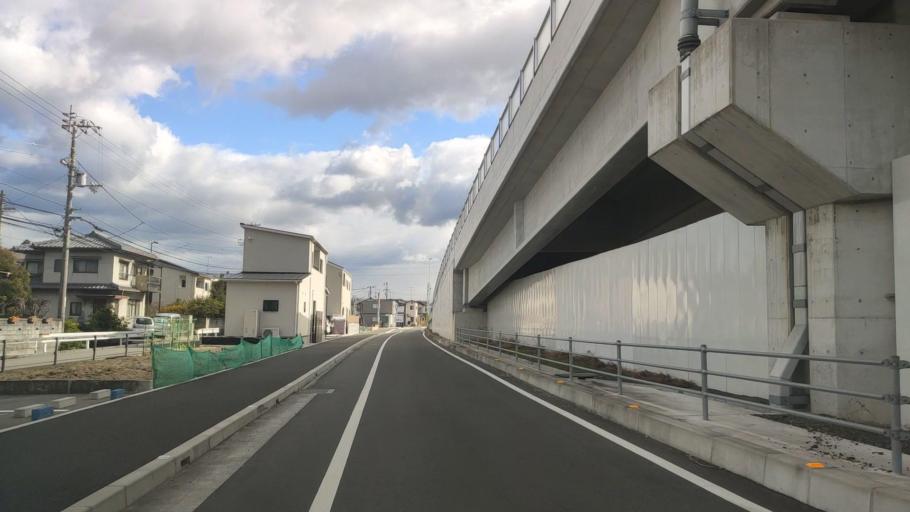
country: JP
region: Ehime
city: Masaki-cho
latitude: 33.8115
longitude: 132.7311
